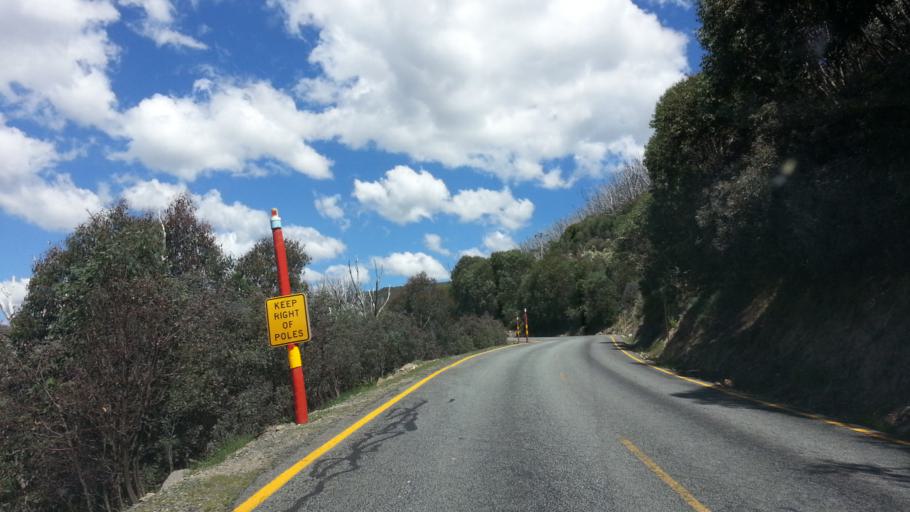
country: AU
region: Victoria
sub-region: Alpine
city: Mount Beauty
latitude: -36.8537
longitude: 147.2723
